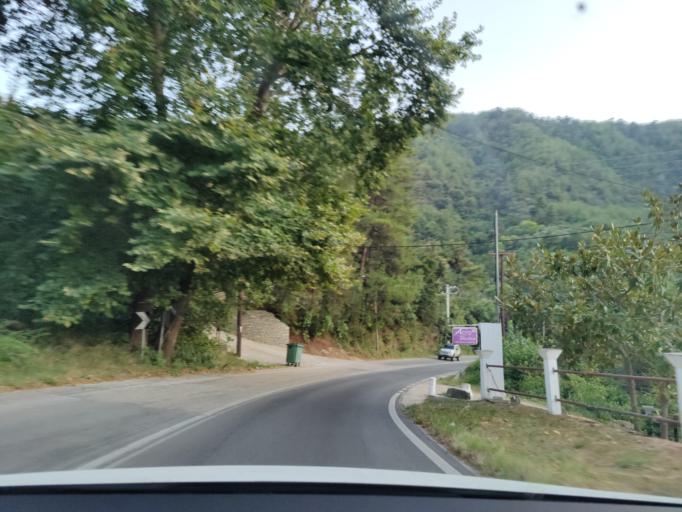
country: GR
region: East Macedonia and Thrace
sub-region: Nomos Kavalas
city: Potamia
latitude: 40.7061
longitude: 24.7635
